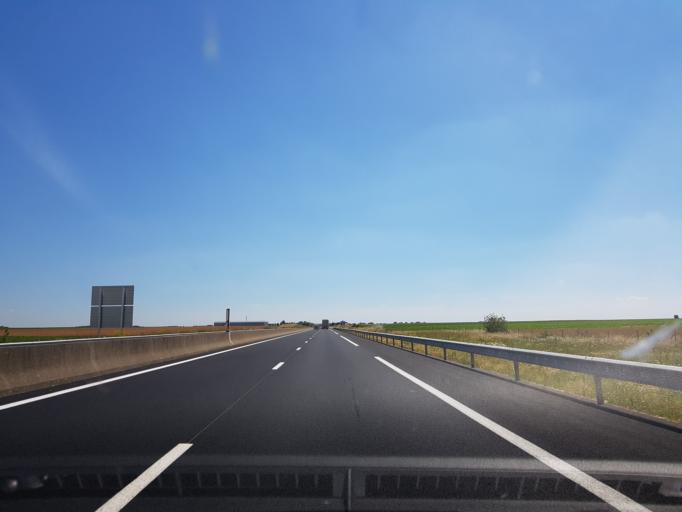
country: FR
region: Picardie
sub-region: Departement de la Somme
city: Doingt
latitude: 49.8370
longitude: 2.9732
